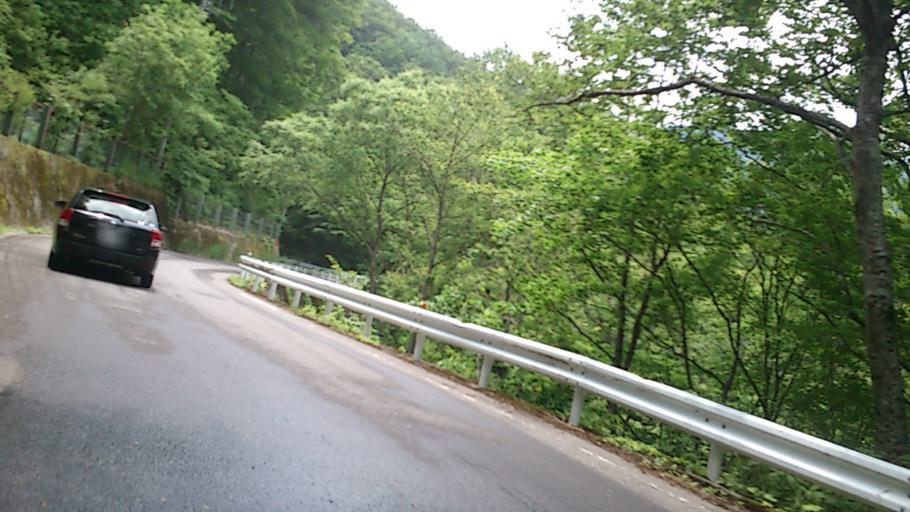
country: JP
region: Aomori
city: Hirosaki
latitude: 40.5179
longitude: 140.1846
